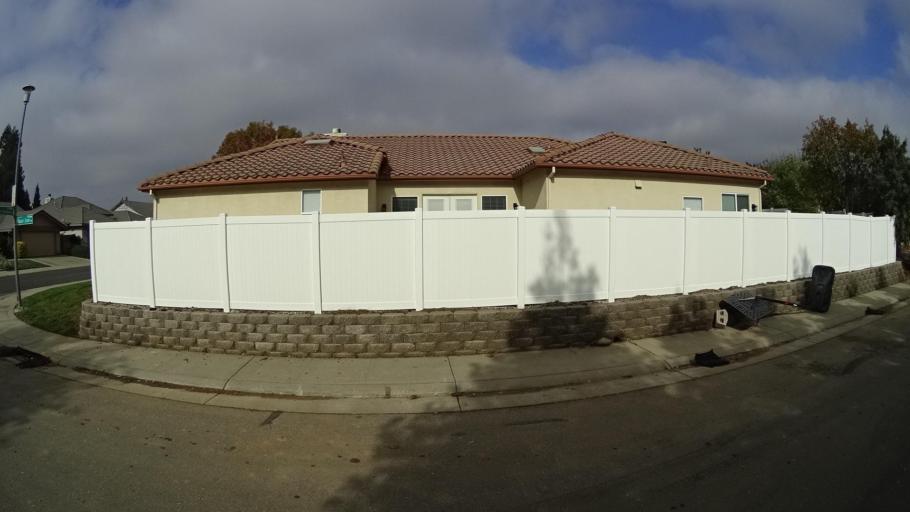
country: US
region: California
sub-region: Sacramento County
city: Elk Grove
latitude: 38.4248
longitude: -121.3626
